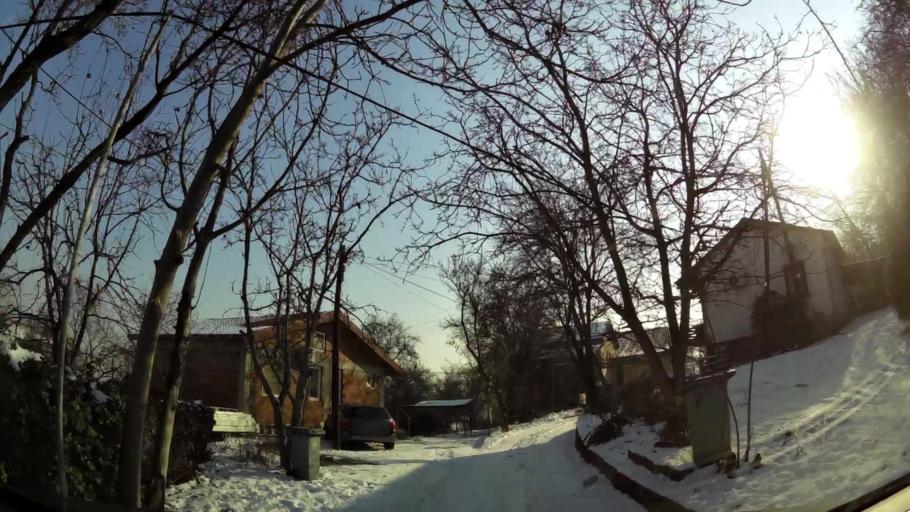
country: MK
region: Karpos
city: Skopje
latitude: 41.9802
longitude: 21.4265
